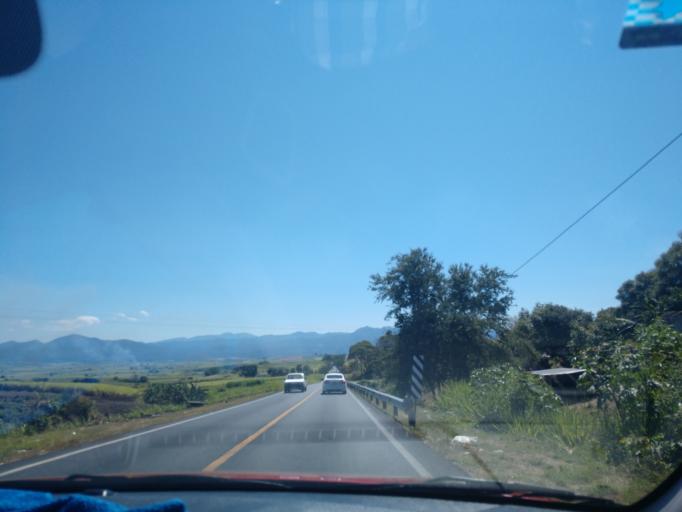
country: MX
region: Nayarit
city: Xalisco
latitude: 21.3940
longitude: -104.8960
